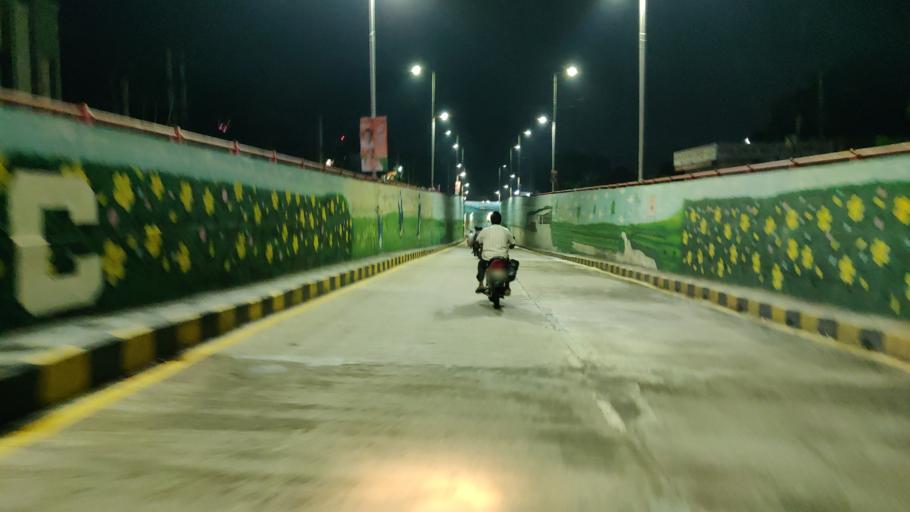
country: IN
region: Telangana
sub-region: Rangareddi
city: Lal Bahadur Nagar
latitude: 17.3420
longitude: 78.5549
